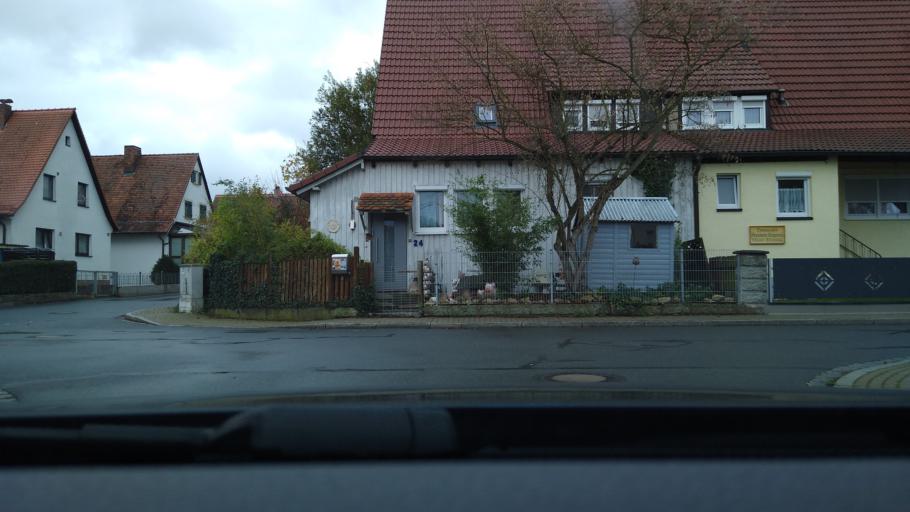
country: DE
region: Bavaria
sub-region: Regierungsbezirk Mittelfranken
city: Hemhofen
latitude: 49.6938
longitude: 10.9387
